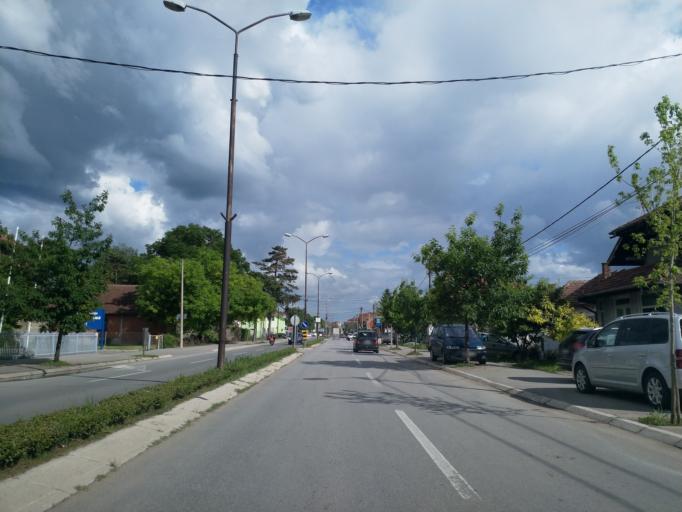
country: RS
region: Central Serbia
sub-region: Pomoravski Okrug
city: Paracin
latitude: 43.8712
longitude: 21.4008
